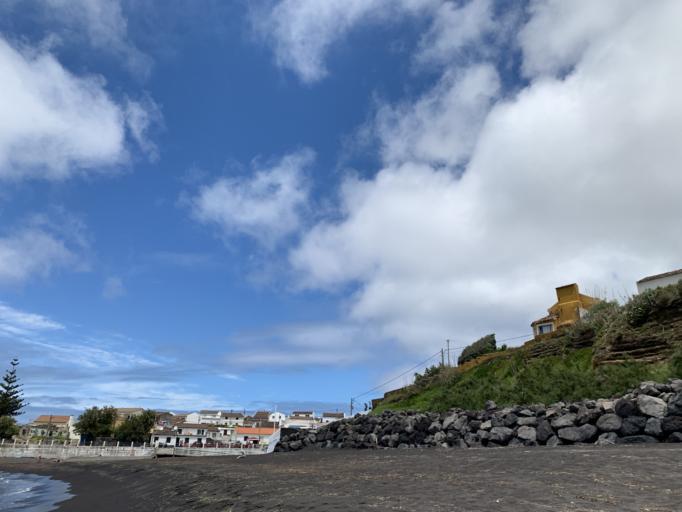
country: PT
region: Azores
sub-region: Ponta Delgada
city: Arrifes
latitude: 37.8876
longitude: -25.8239
